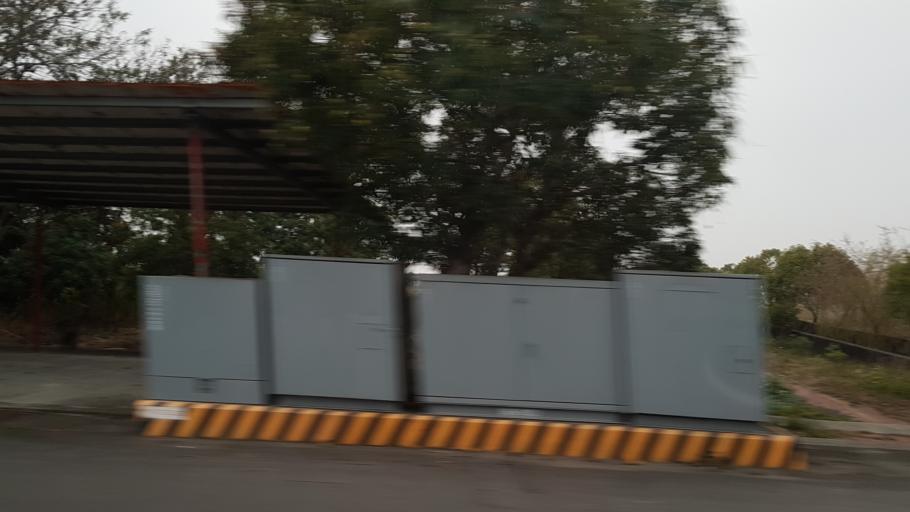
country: TW
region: Taiwan
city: Xinying
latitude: 23.3278
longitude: 120.3162
